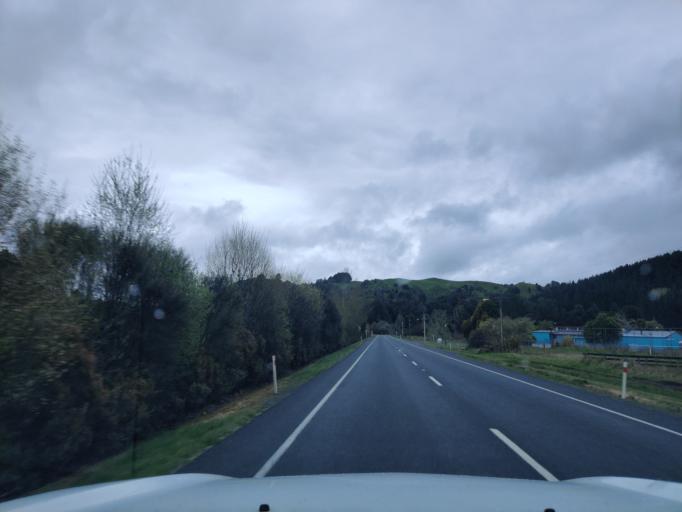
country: NZ
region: Waikato
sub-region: Otorohanga District
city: Otorohanga
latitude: -38.5770
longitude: 175.2144
